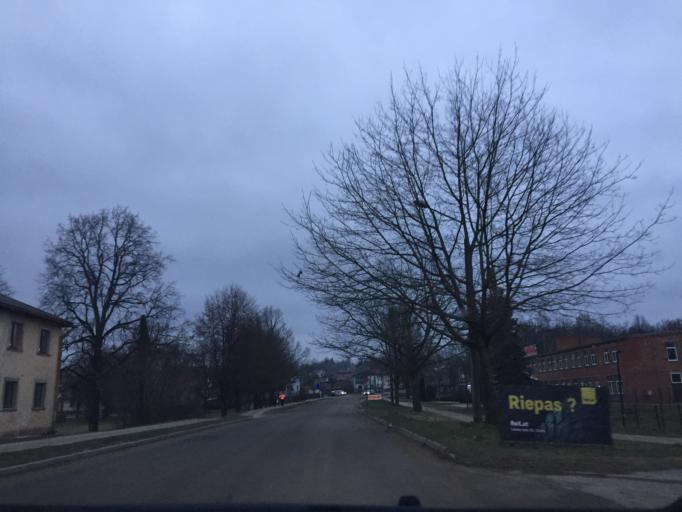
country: LV
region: Cesu Rajons
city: Cesis
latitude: 57.3201
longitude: 25.2646
